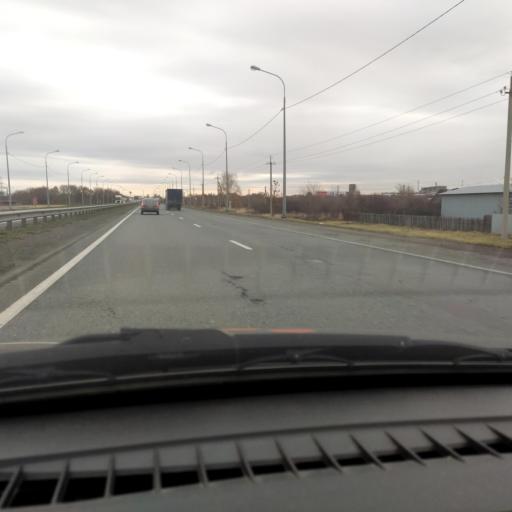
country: RU
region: Samara
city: Tol'yatti
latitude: 53.5746
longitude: 49.4448
